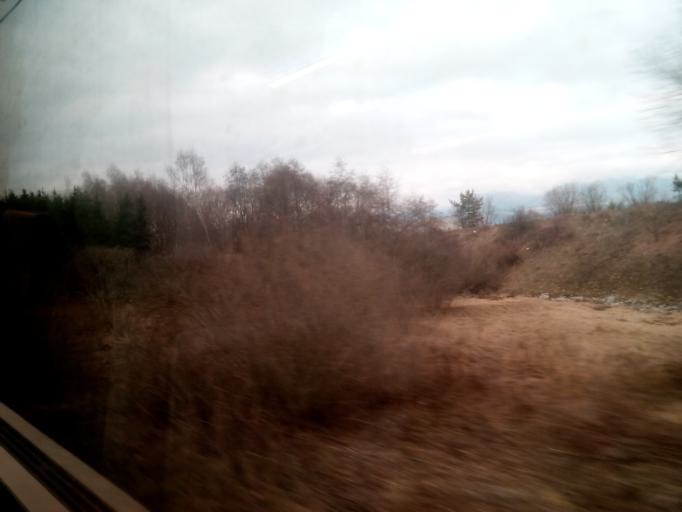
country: SK
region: Zilinsky
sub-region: Okres Liptovsky Mikulas
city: Liptovsky Mikulas
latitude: 49.0830
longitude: 19.5742
